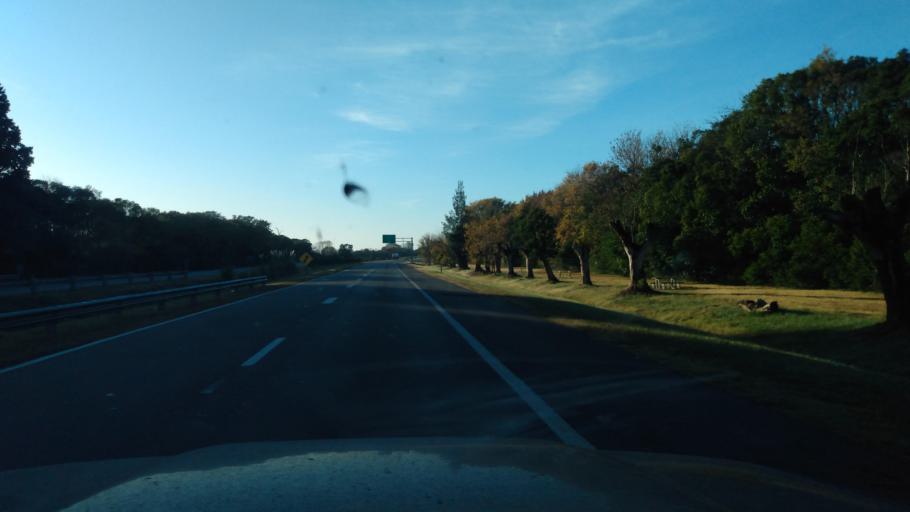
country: AR
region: Buenos Aires
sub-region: Partido de Lujan
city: Lujan
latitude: -34.5472
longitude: -59.2047
